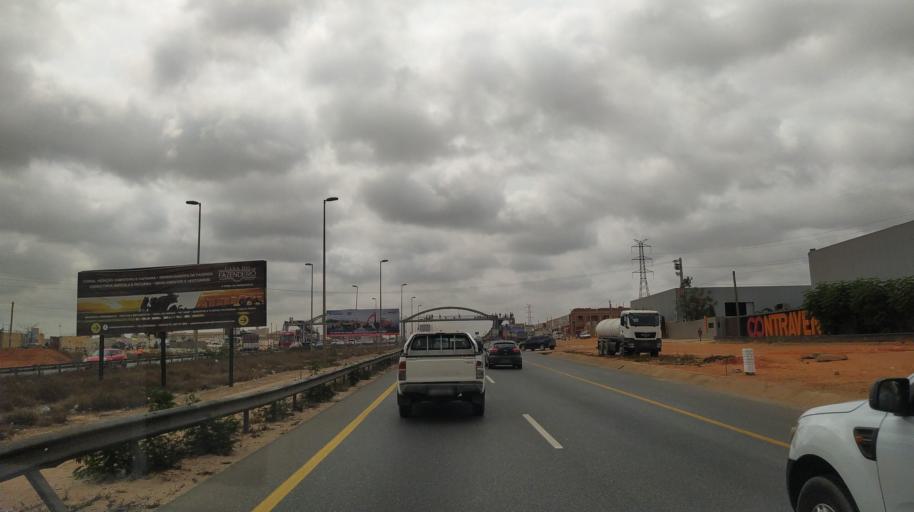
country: AO
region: Luanda
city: Luanda
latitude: -8.9731
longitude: 13.3042
